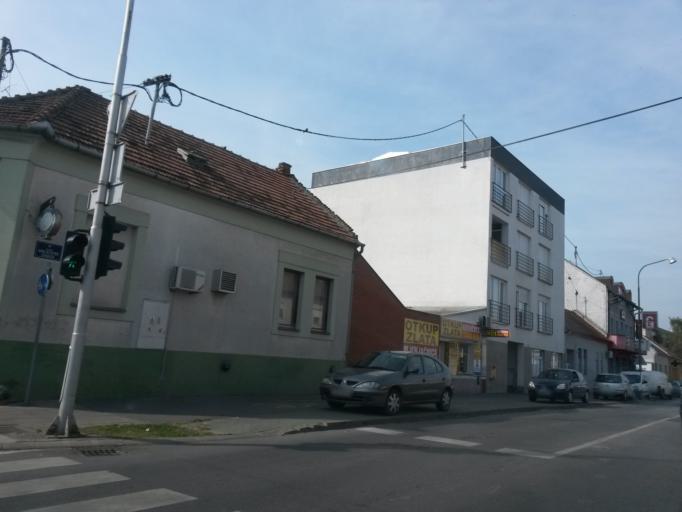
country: HR
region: Osjecko-Baranjska
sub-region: Grad Osijek
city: Osijek
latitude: 45.5504
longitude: 18.7059
